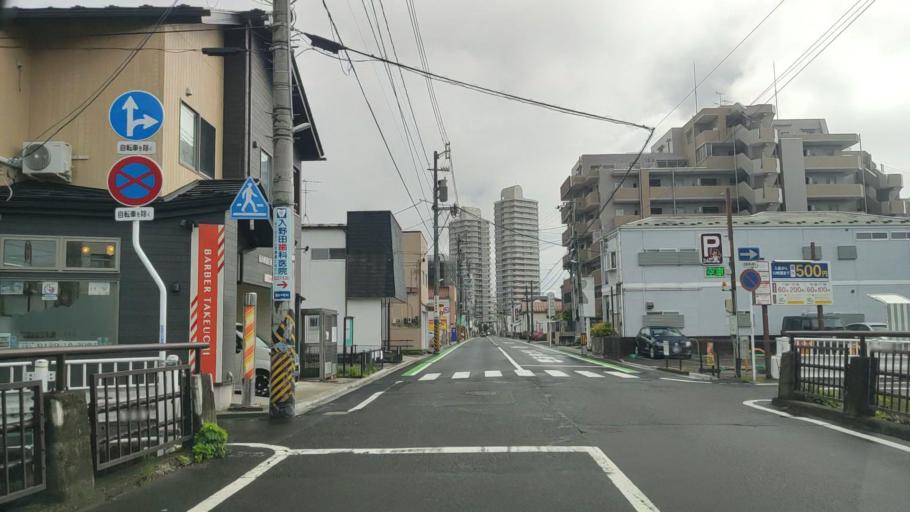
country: JP
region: Miyagi
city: Sendai
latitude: 38.2433
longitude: 140.8891
